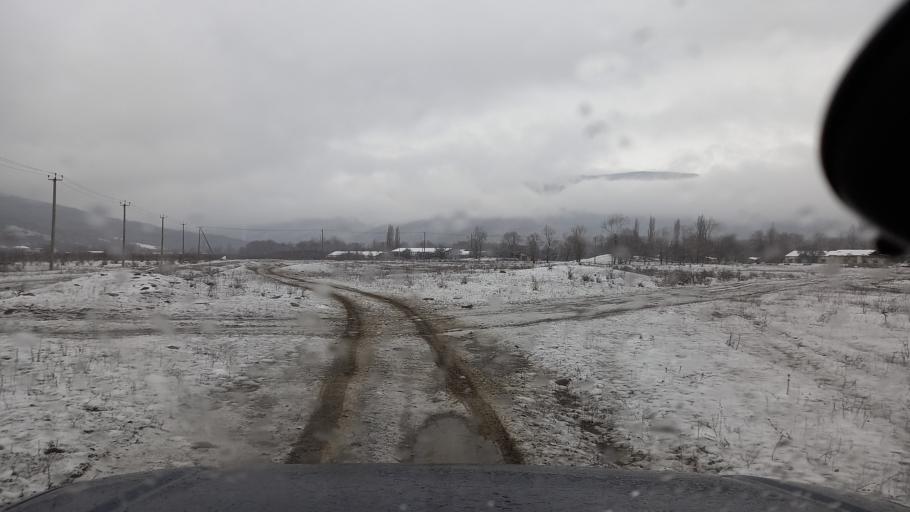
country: RU
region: Adygeya
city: Kamennomostskiy
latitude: 44.2208
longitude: 40.1798
